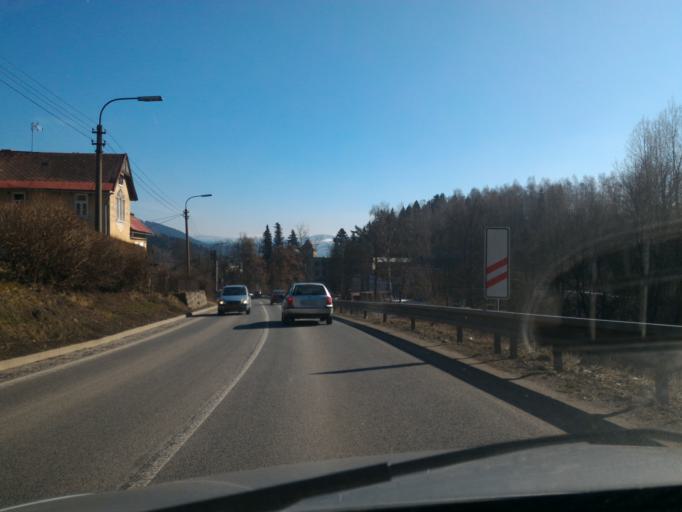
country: CZ
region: Liberecky
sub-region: Okres Jablonec nad Nisou
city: Smrzovka
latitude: 50.7382
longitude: 15.2357
